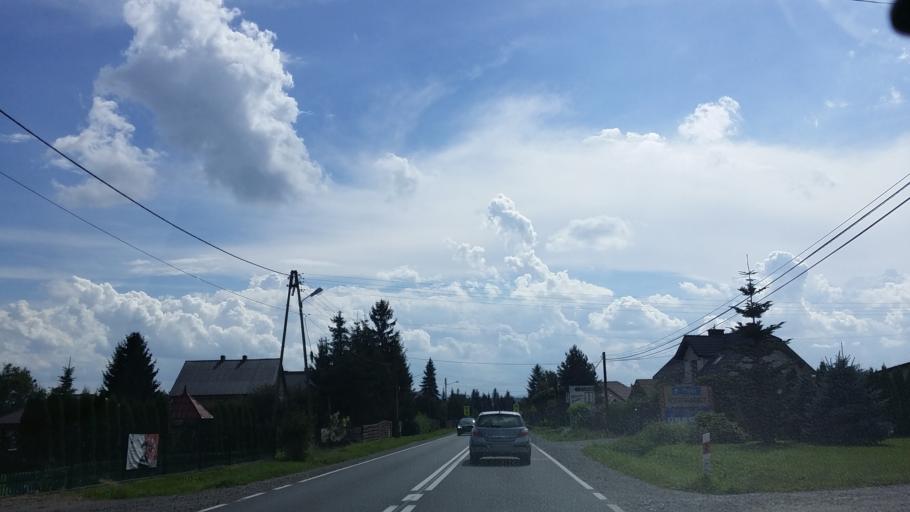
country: PL
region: Lesser Poland Voivodeship
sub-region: Powiat wielicki
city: Pawlikowice
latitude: 49.9637
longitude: 20.0570
